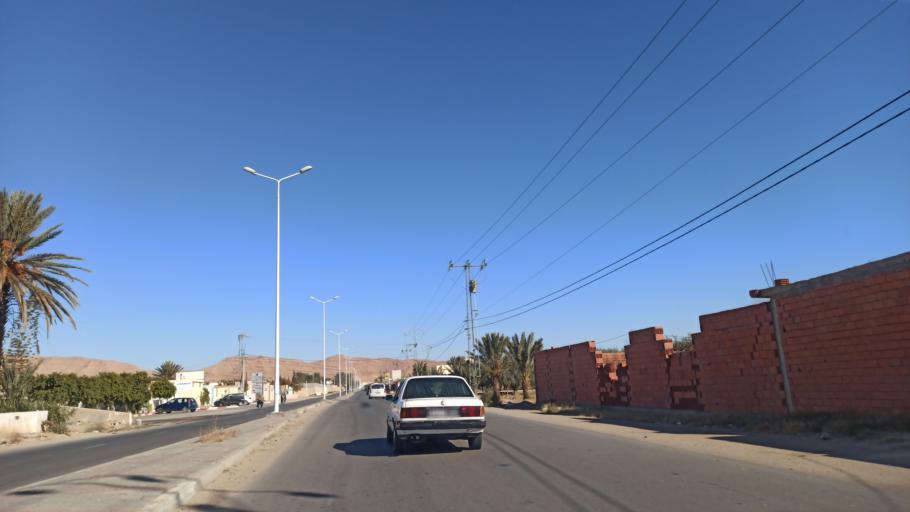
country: TN
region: Gafsa
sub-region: Gafsa Municipality
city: Gafsa
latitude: 34.4091
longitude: 8.7359
